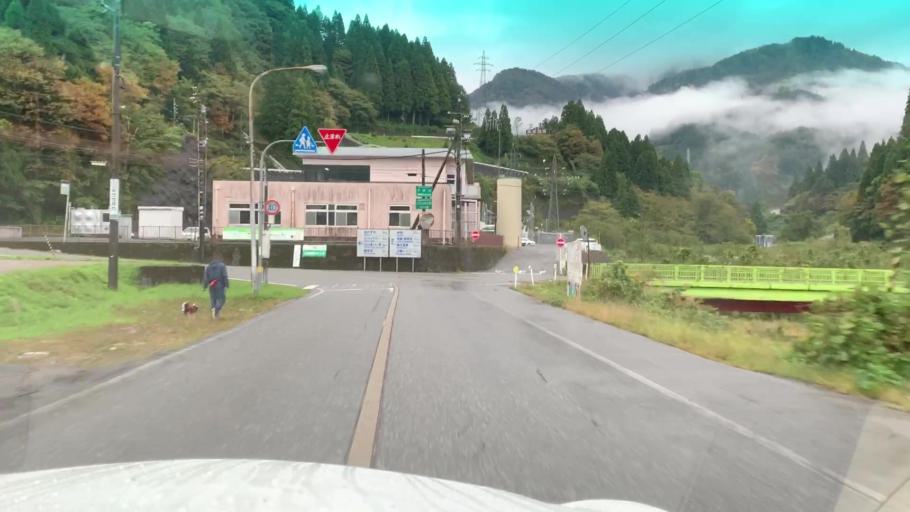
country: JP
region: Toyama
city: Kamiichi
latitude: 36.5712
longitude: 137.3818
